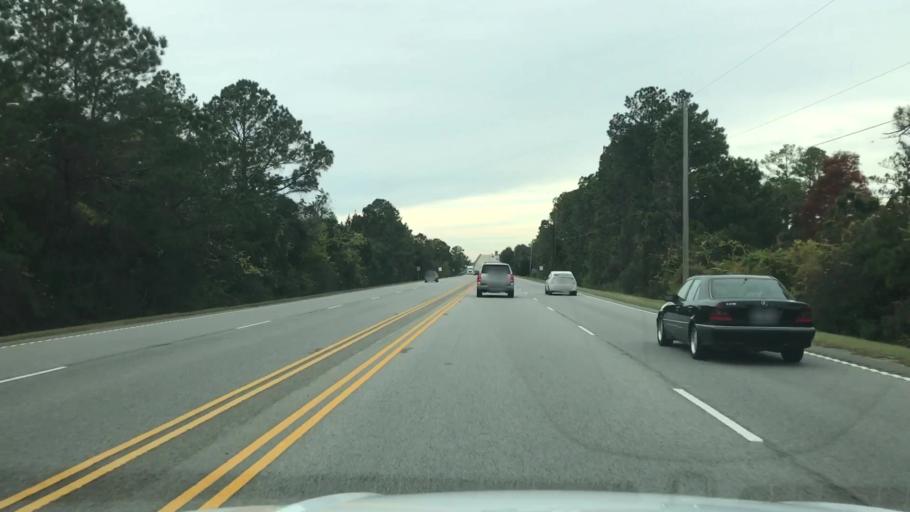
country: US
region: South Carolina
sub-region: Georgetown County
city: Georgetown
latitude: 33.3648
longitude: -79.2433
